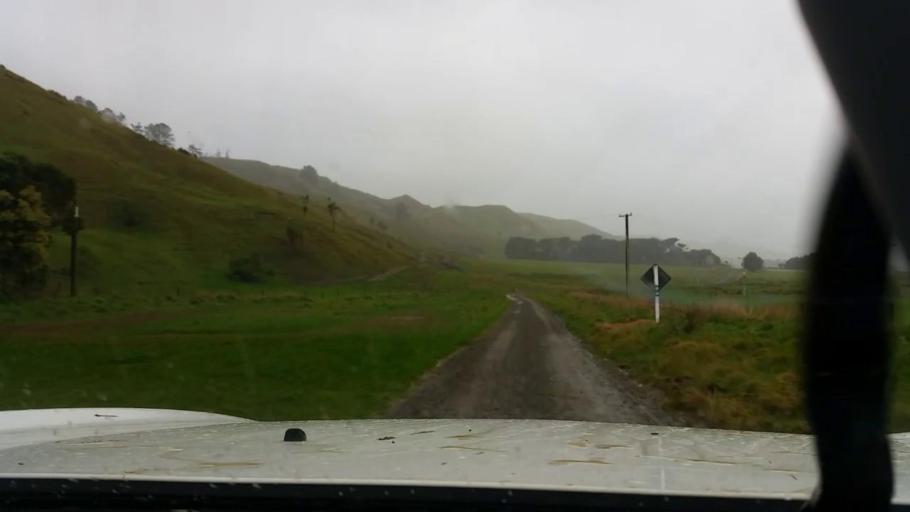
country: NZ
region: Wellington
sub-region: Masterton District
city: Masterton
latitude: -41.2607
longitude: 175.8968
